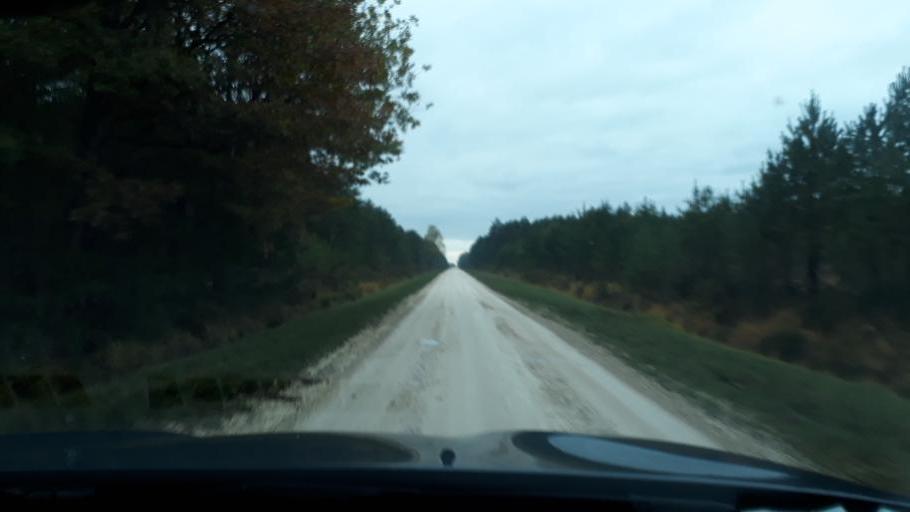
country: FR
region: Centre
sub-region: Departement du Loiret
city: Bouzy-la-Foret
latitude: 47.8427
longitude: 2.4459
